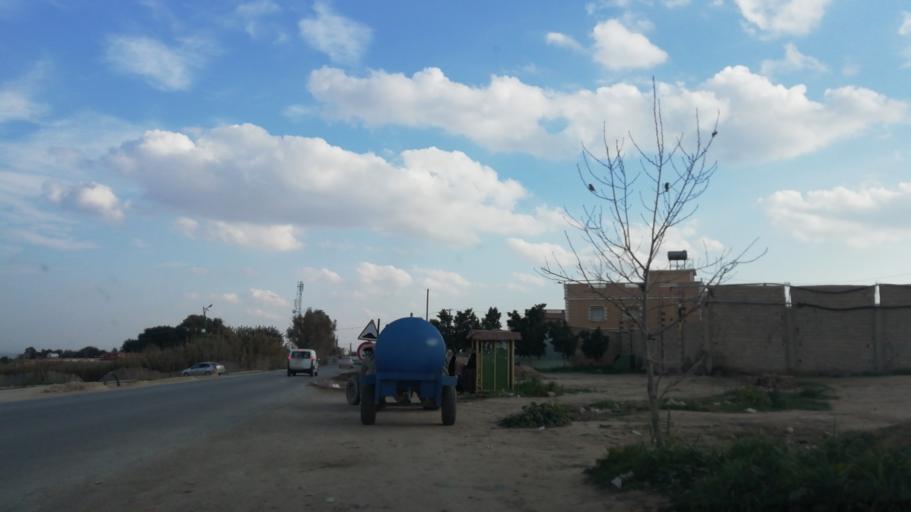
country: DZ
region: Relizane
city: Relizane
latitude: 35.9114
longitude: 0.5041
